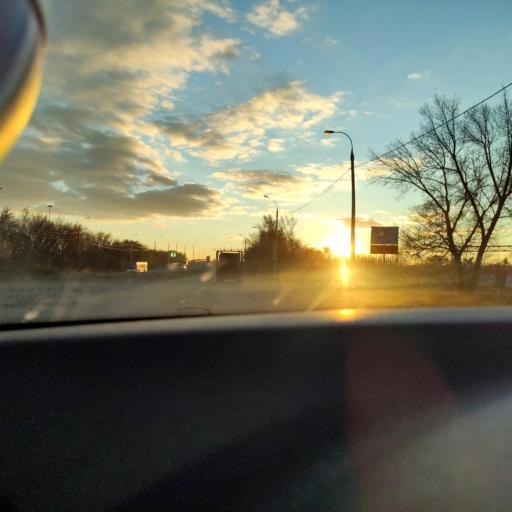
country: RU
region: Samara
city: Smyshlyayevka
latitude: 53.2558
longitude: 50.3714
